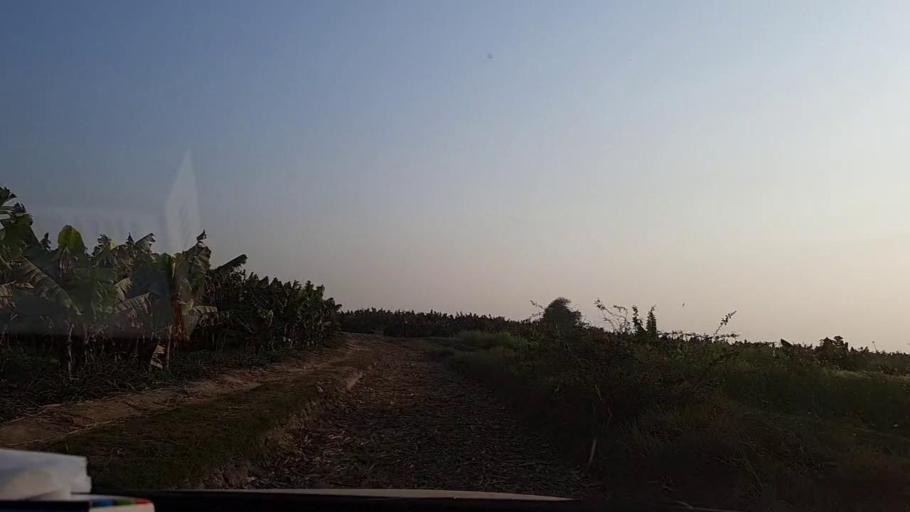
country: PK
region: Sindh
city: Tando Ghulam Ali
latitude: 25.1957
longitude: 68.9147
